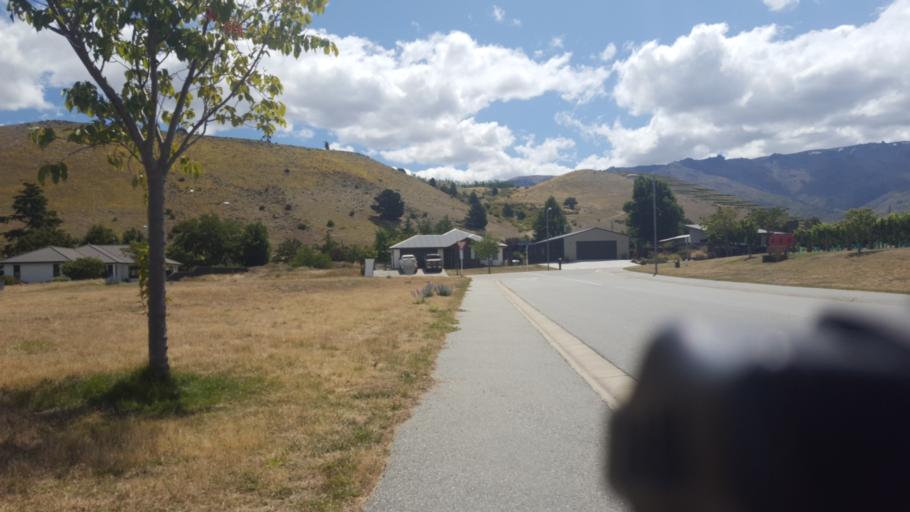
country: NZ
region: Otago
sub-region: Queenstown-Lakes District
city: Wanaka
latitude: -44.9792
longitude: 169.2367
